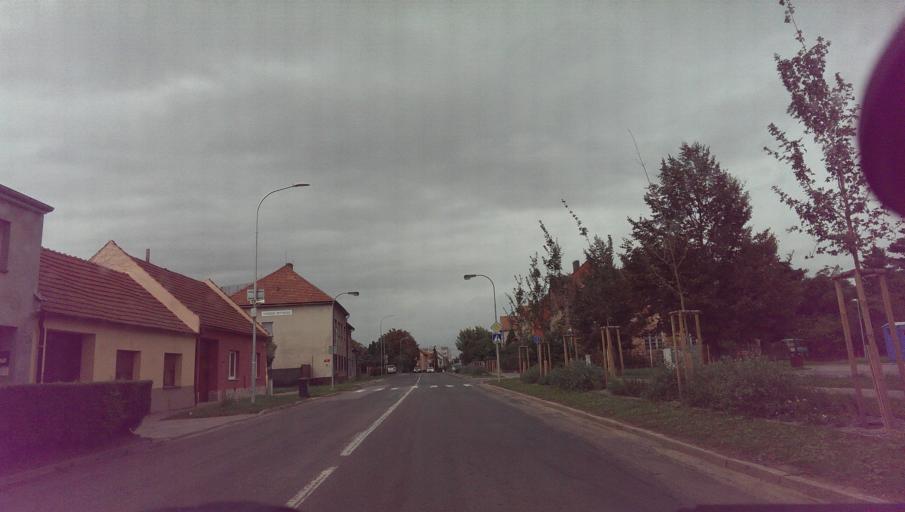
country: CZ
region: South Moravian
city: Veseli nad Moravou
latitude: 48.9588
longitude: 17.3886
